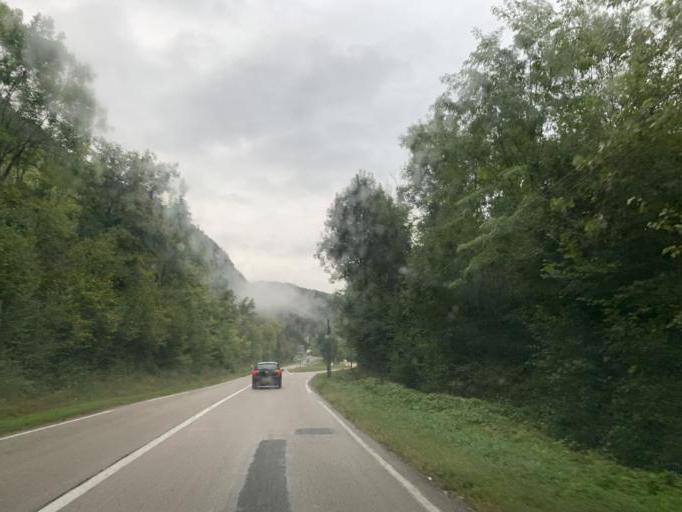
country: FR
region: Rhone-Alpes
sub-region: Departement de l'Isere
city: Les Avenieres
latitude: 45.6745
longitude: 5.6080
